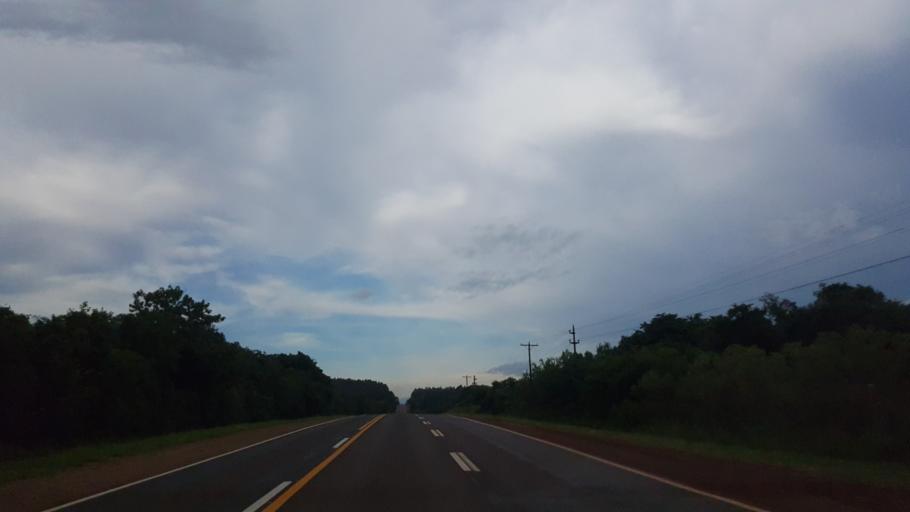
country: AR
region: Misiones
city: Jardin America
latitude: -27.0802
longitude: -55.2827
